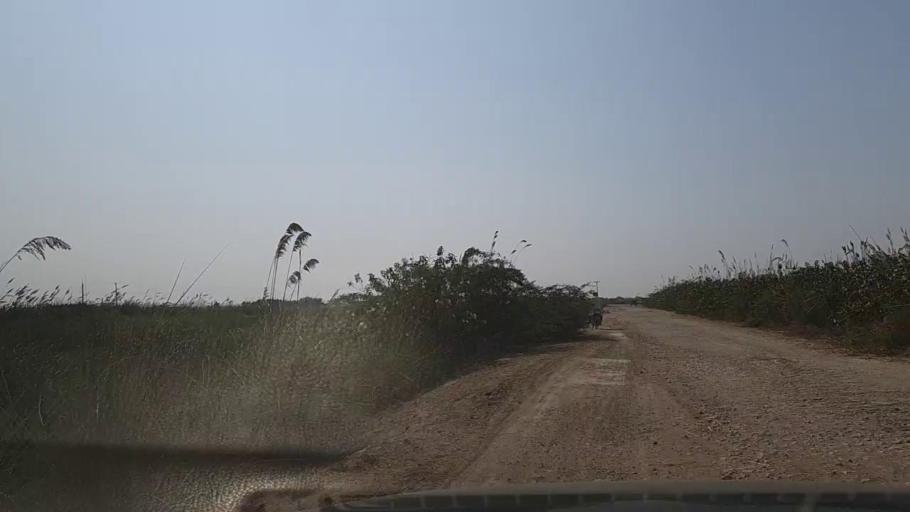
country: PK
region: Sindh
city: Mirpur Sakro
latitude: 24.3687
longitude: 67.6477
